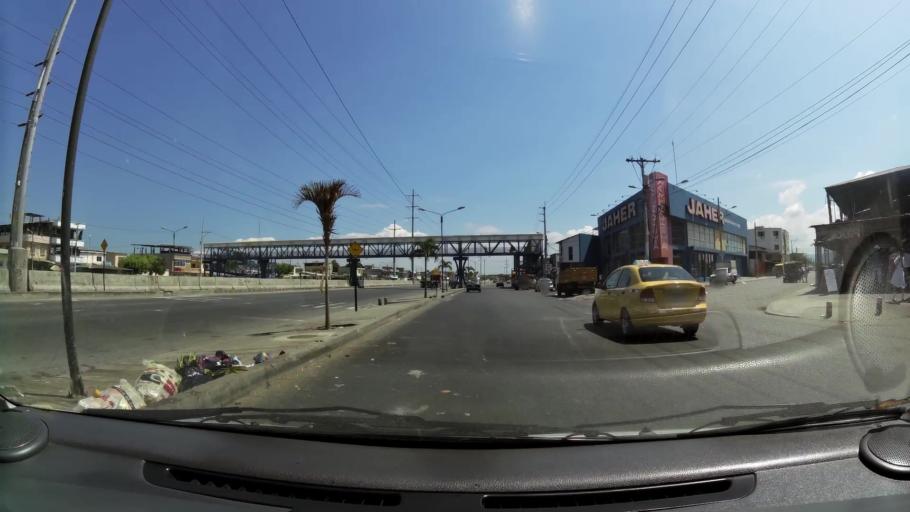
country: EC
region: Guayas
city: Guayaquil
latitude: -2.2398
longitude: -79.9195
